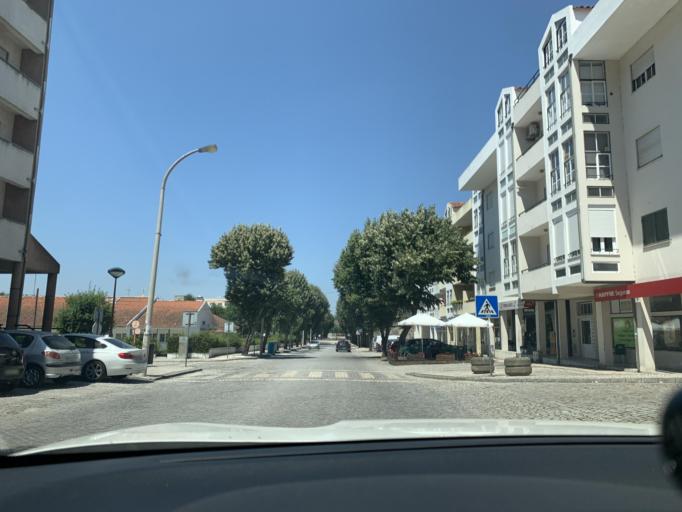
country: PT
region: Viseu
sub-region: Nelas
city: Nelas
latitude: 40.5317
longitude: -7.8544
